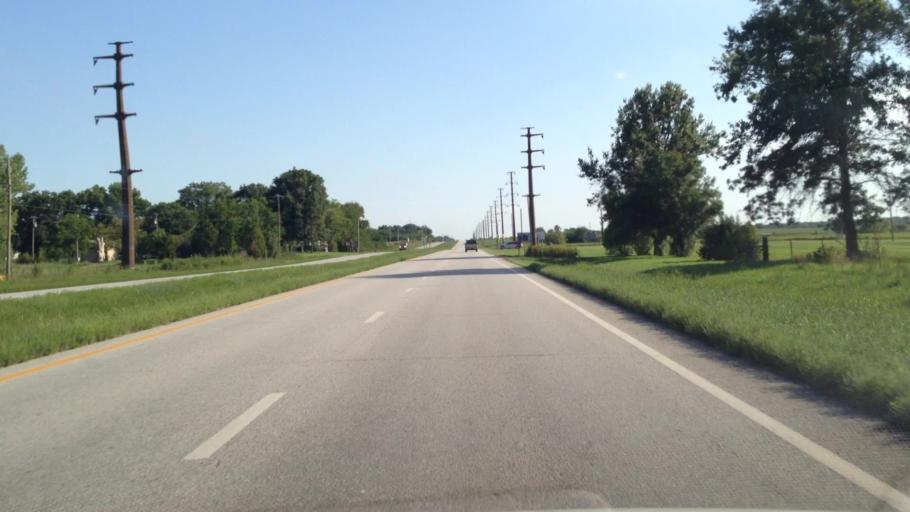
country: US
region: Kansas
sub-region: Crawford County
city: Arma
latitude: 37.5007
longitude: -94.7053
